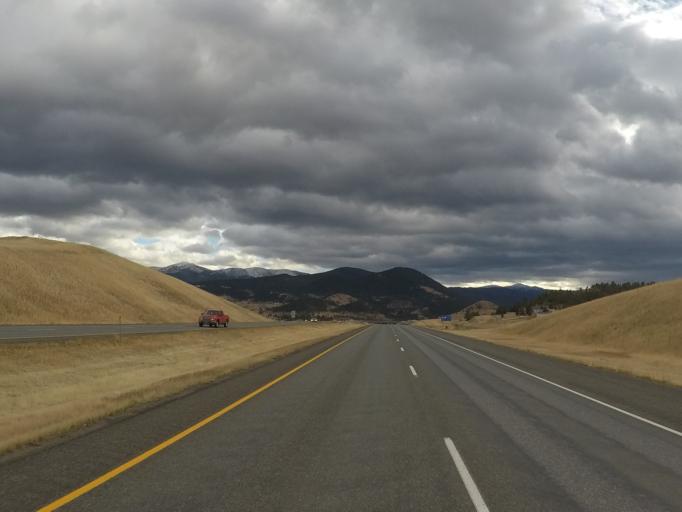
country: US
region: Montana
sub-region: Jefferson County
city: Montana City
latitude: 46.5512
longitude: -111.9499
